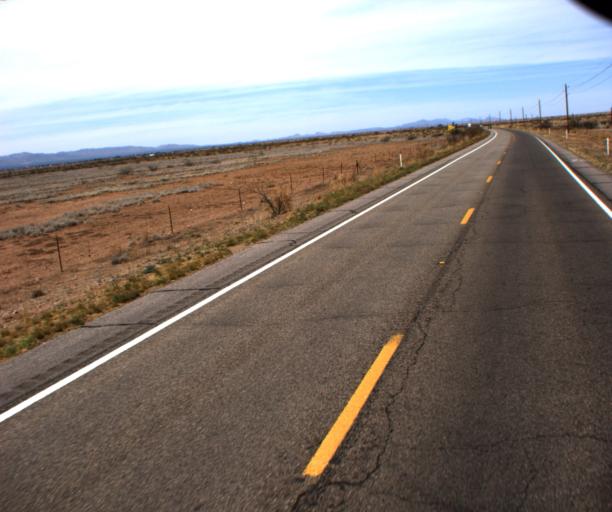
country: US
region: Arizona
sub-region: Cochise County
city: Pirtleville
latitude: 31.4306
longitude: -109.5861
